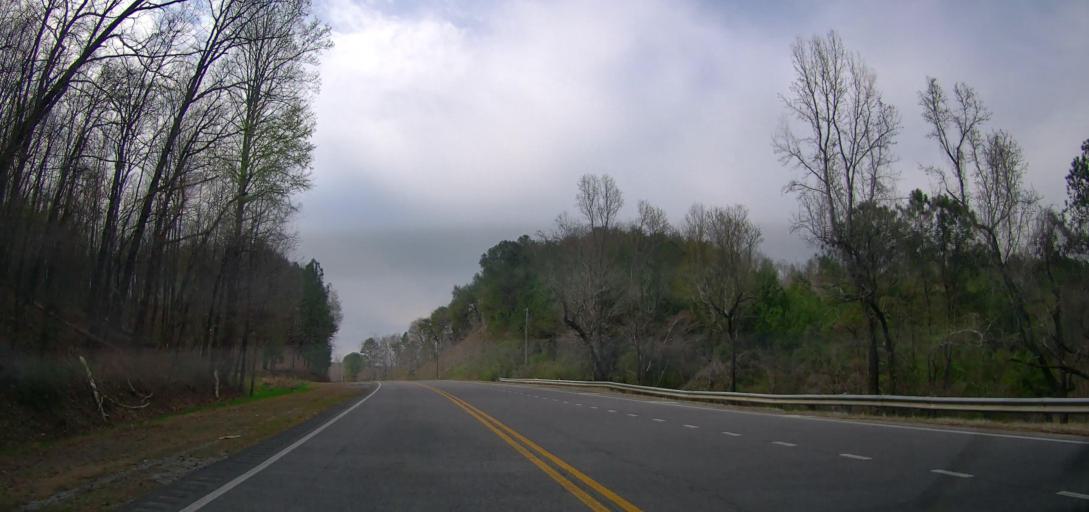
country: US
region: Alabama
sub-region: Walker County
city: Carbon Hill
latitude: 33.9164
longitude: -87.5673
